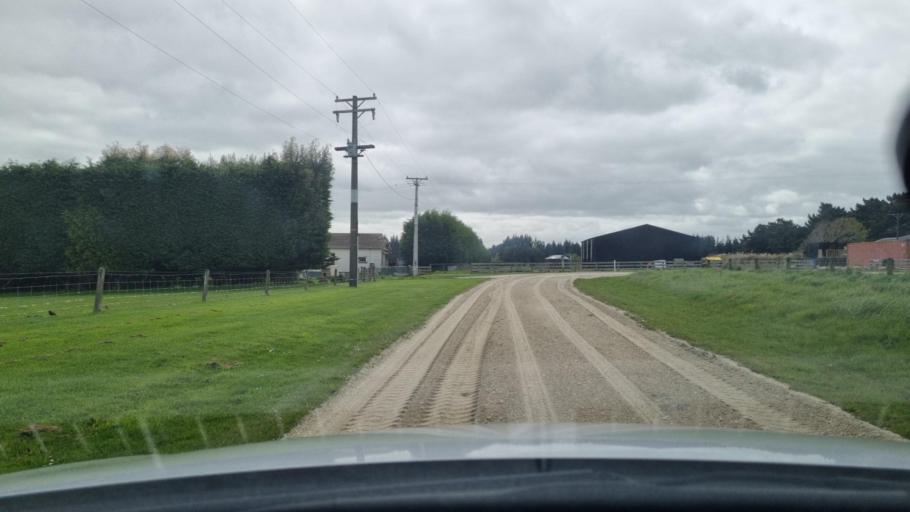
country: NZ
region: Southland
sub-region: Invercargill City
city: Invercargill
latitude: -46.4322
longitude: 168.4107
